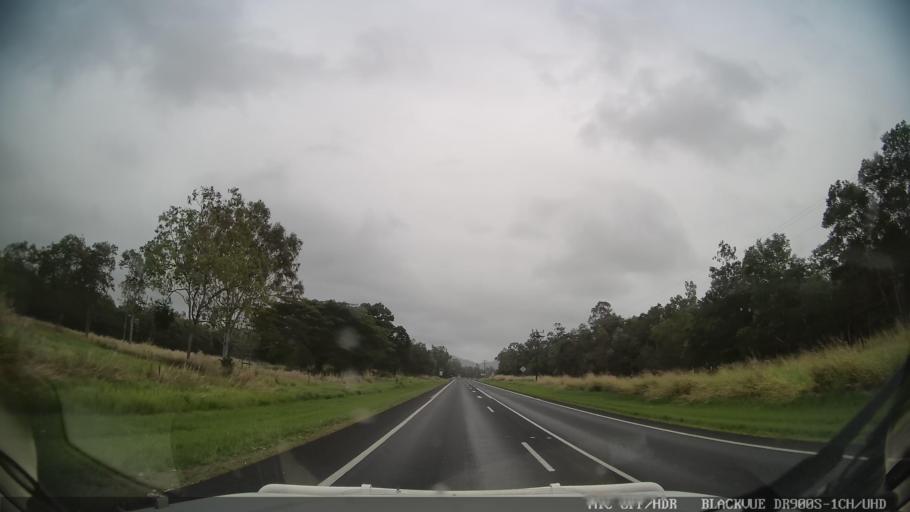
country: AU
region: Queensland
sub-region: Hinchinbrook
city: Ingham
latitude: -18.2046
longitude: 145.9556
